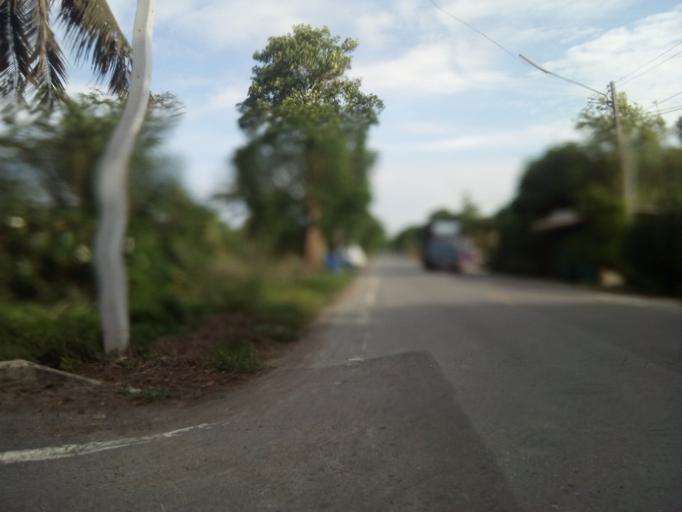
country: TH
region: Pathum Thani
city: Nong Suea
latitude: 14.0923
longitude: 100.8461
